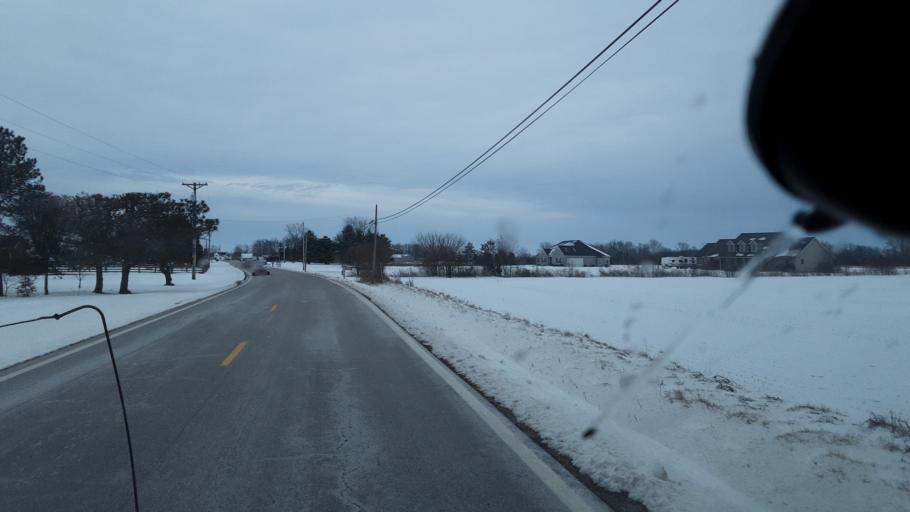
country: US
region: Ohio
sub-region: Pickaway County
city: Williamsport
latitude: 39.6689
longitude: -83.1641
